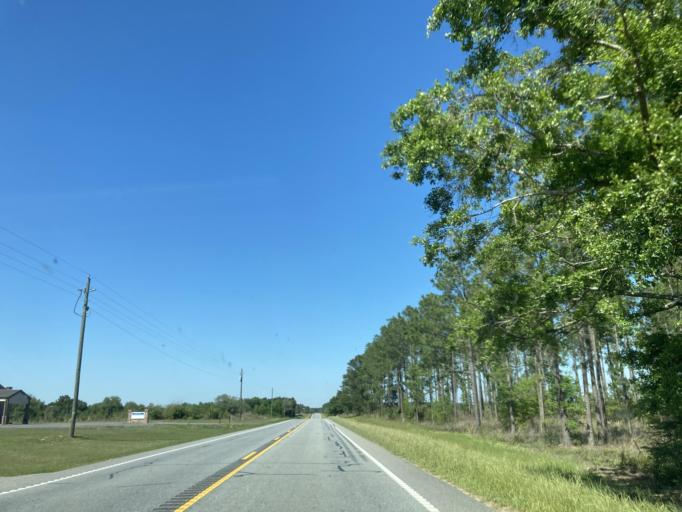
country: US
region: Georgia
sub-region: Baker County
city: Newton
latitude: 31.2315
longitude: -84.4407
